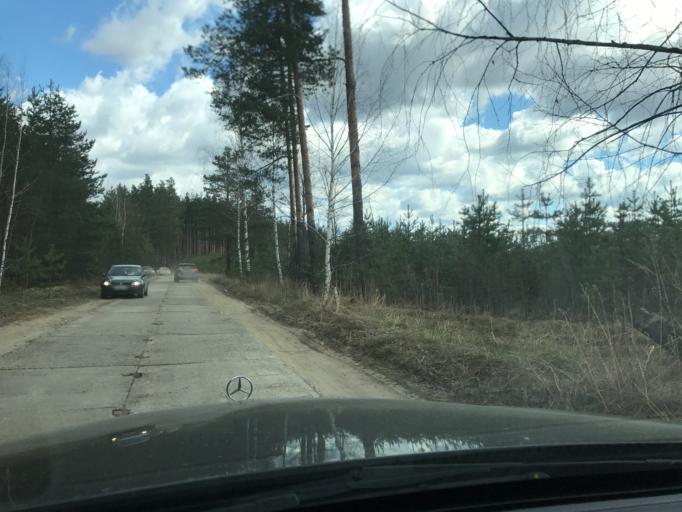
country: RU
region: Vladimir
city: Pokrov
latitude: 55.8435
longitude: 39.1430
